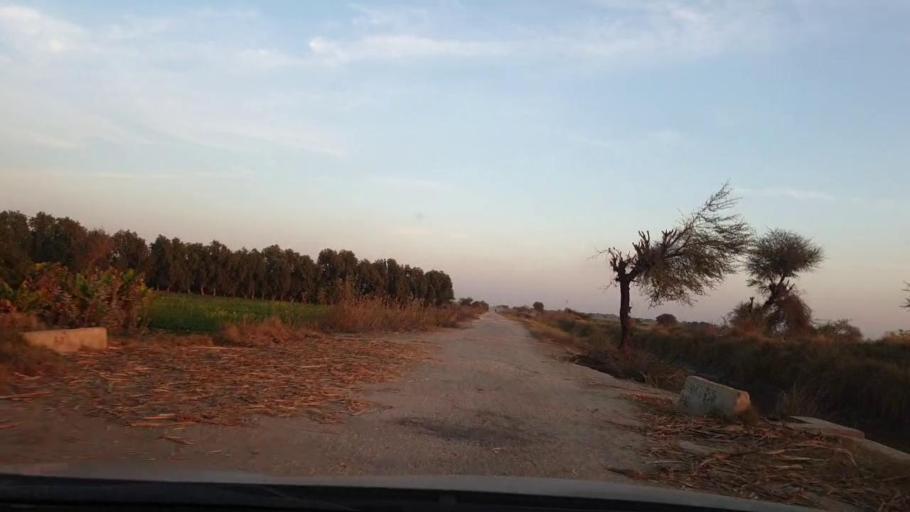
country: PK
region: Sindh
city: Tando Allahyar
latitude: 25.5844
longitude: 68.7217
